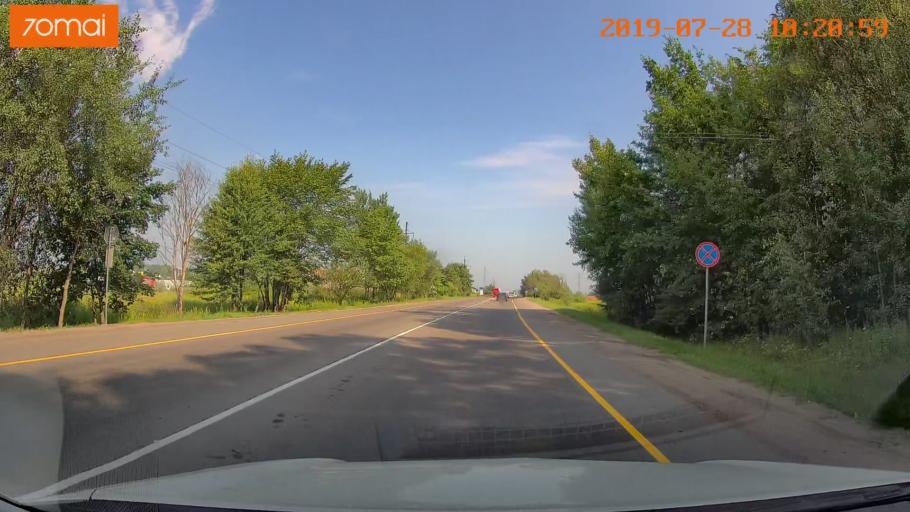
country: RU
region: Kaliningrad
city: Maloye Isakovo
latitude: 54.7531
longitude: 20.5658
